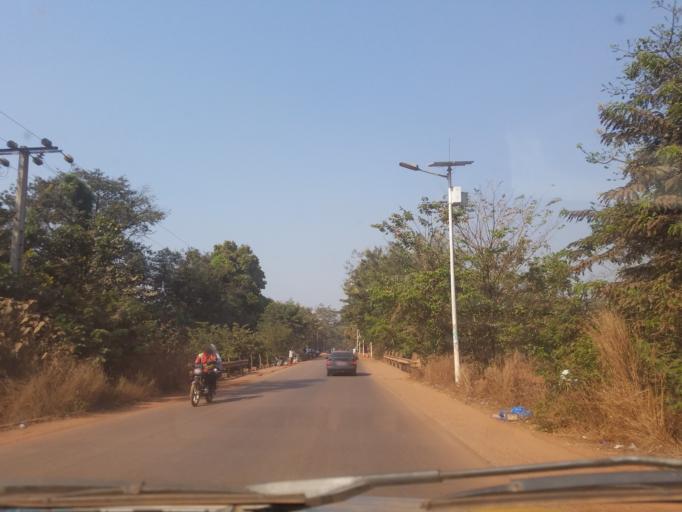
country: GN
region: Boke
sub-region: Boke Prefecture
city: Boke
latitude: 10.9213
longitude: -14.2954
